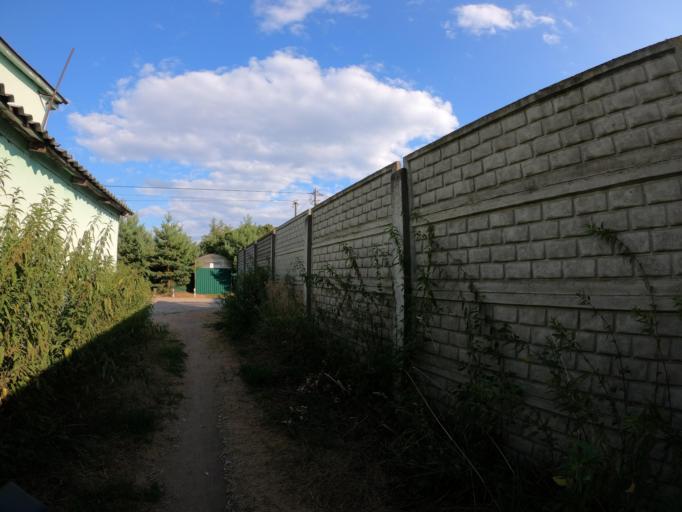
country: RU
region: Moskovskaya
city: Bronnitsy
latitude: 55.4707
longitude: 38.2562
